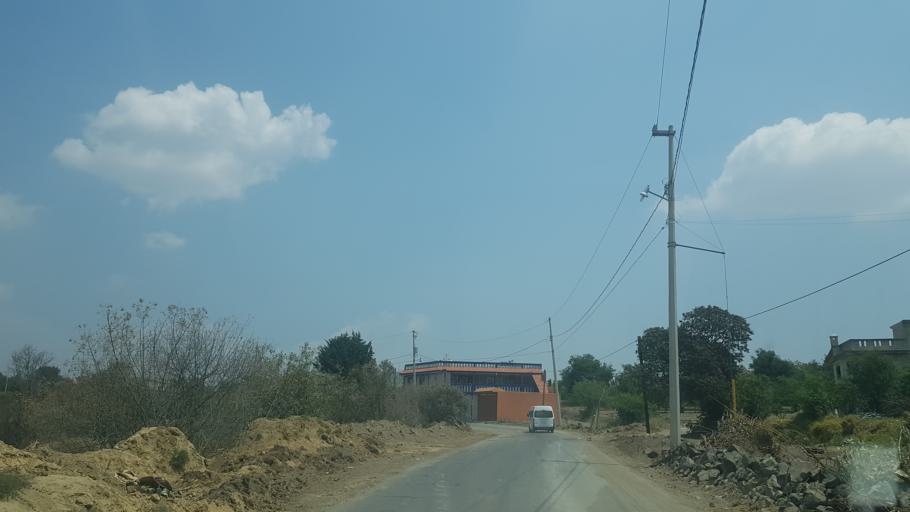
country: MX
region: Puebla
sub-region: San Nicolas de los Ranchos
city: San Pedro Yancuitlalpan
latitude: 19.0808
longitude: -98.4804
